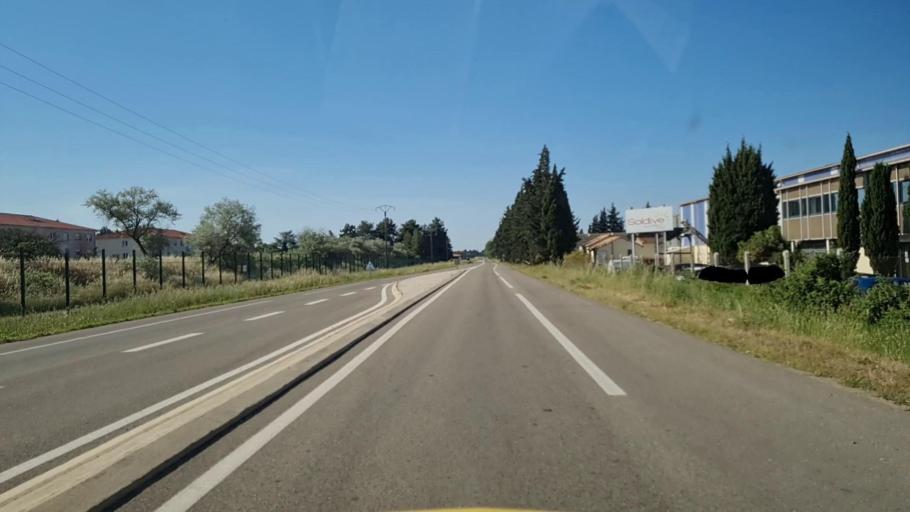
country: FR
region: Languedoc-Roussillon
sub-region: Departement du Gard
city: Garons
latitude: 43.7645
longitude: 4.4056
